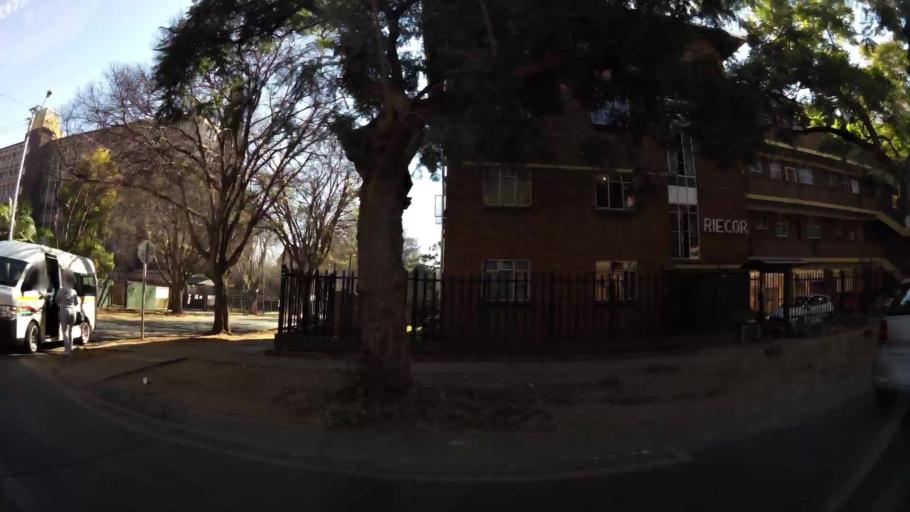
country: ZA
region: Gauteng
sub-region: City of Tshwane Metropolitan Municipality
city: Pretoria
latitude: -25.7592
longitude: 28.2095
